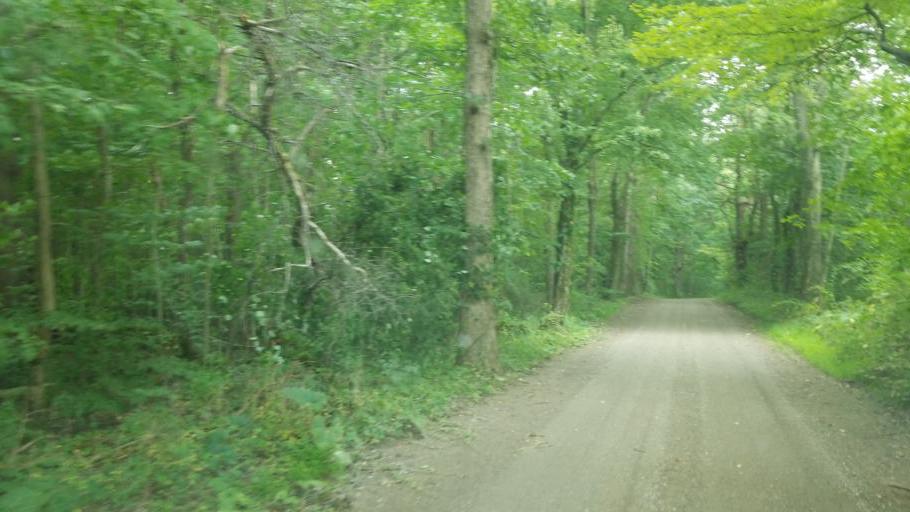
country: US
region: Ohio
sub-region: Ashland County
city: Loudonville
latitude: 40.5946
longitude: -82.3009
